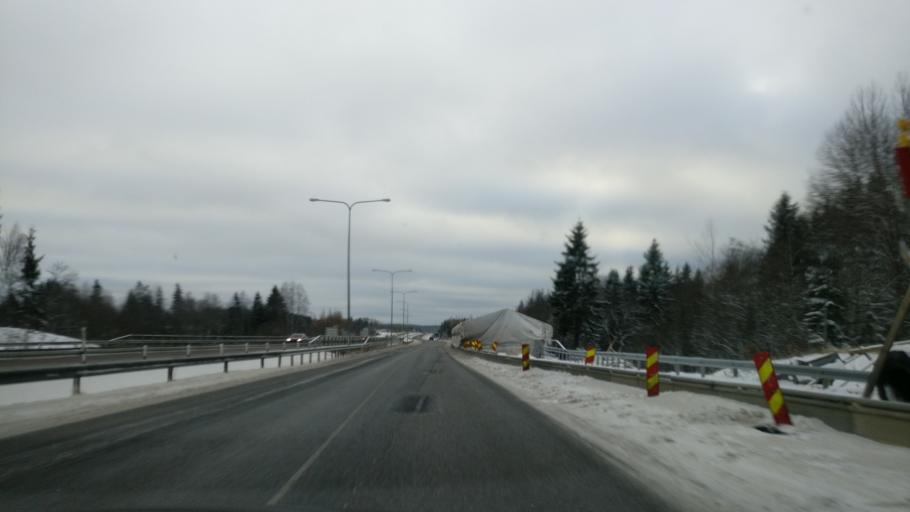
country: FI
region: Paijanne Tavastia
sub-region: Lahti
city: Lahti
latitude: 60.9262
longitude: 25.6310
